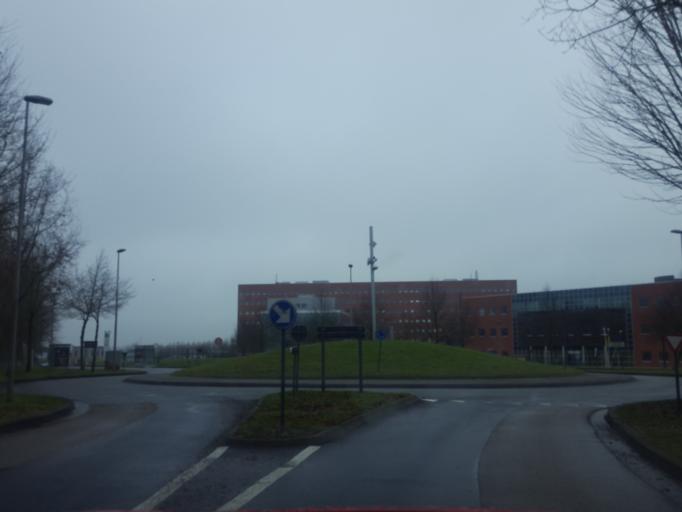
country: BE
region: Flanders
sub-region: Provincie West-Vlaanderen
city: Ieper
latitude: 50.8681
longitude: 2.8924
